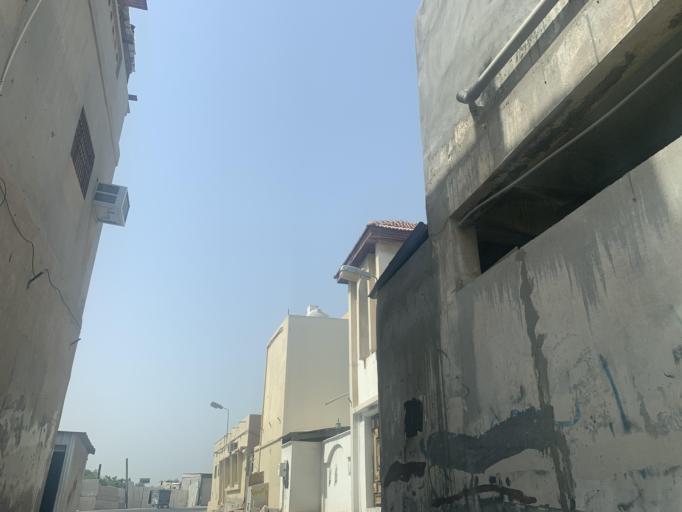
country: BH
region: Manama
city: Jidd Hafs
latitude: 26.2116
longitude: 50.4617
